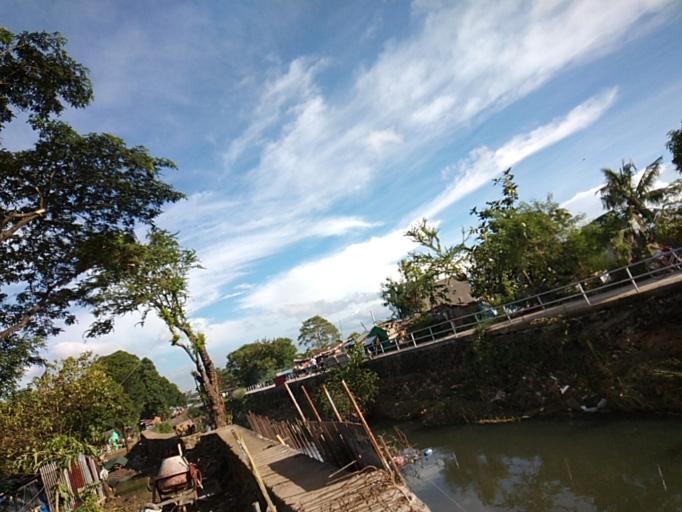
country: PH
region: Calabarzon
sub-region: Province of Rizal
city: Taytay
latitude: 14.5591
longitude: 121.1264
